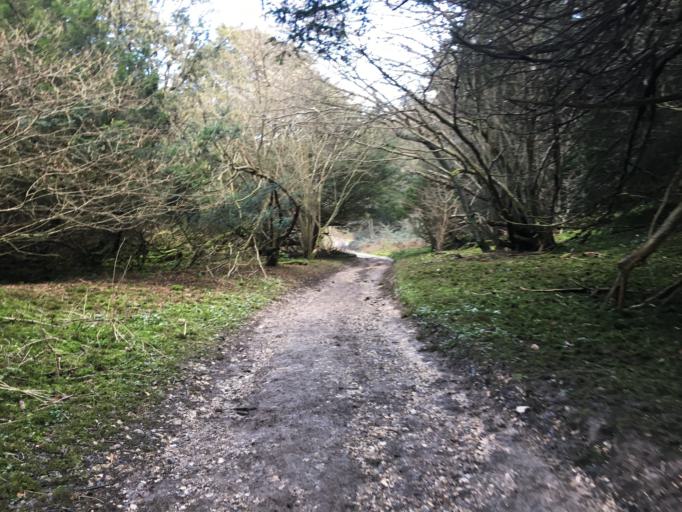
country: GB
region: England
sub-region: Surrey
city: Mickleham
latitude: 51.2554
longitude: -0.3076
